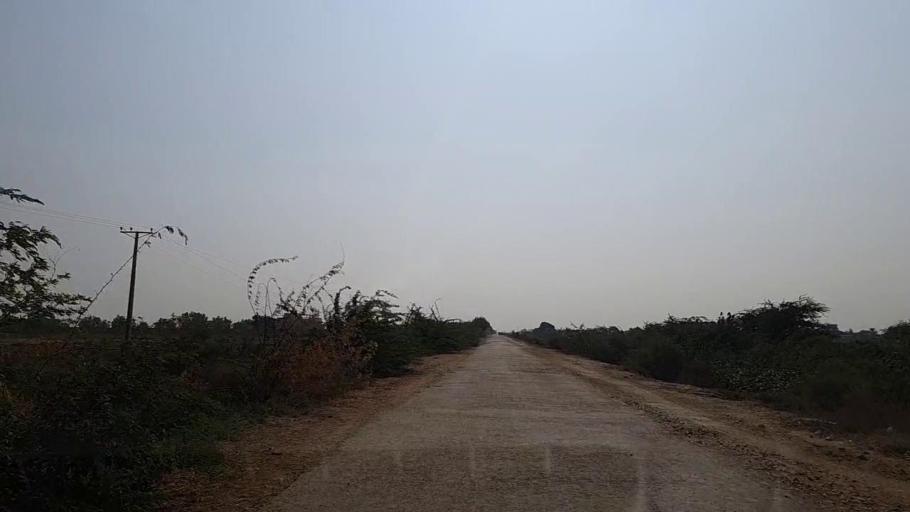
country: PK
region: Sindh
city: Thatta
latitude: 24.7281
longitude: 67.7684
